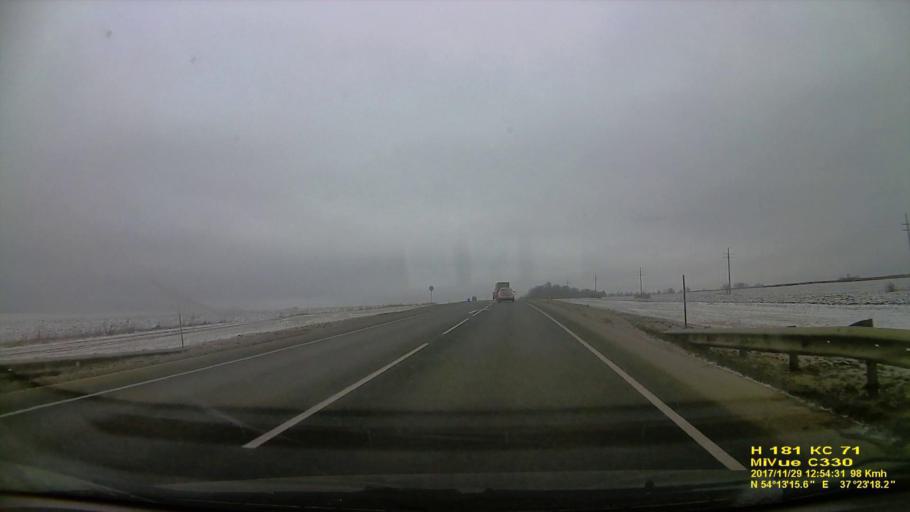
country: RU
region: Tula
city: Leninskiy
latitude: 54.2210
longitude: 37.3883
